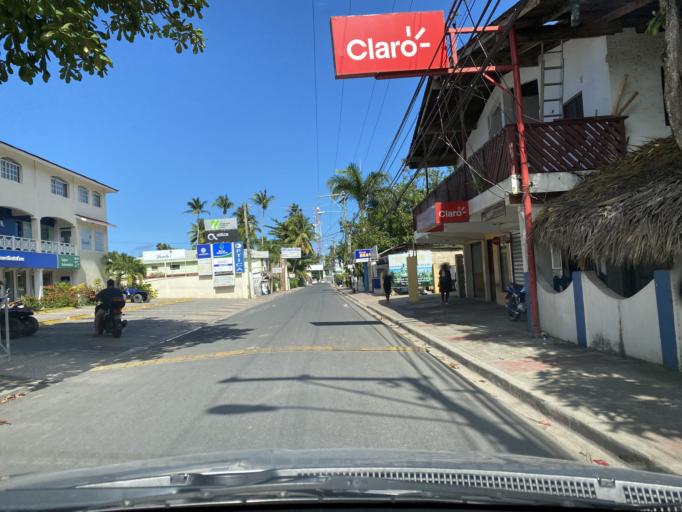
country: DO
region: Samana
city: Las Terrenas
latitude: 19.3178
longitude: -69.5401
